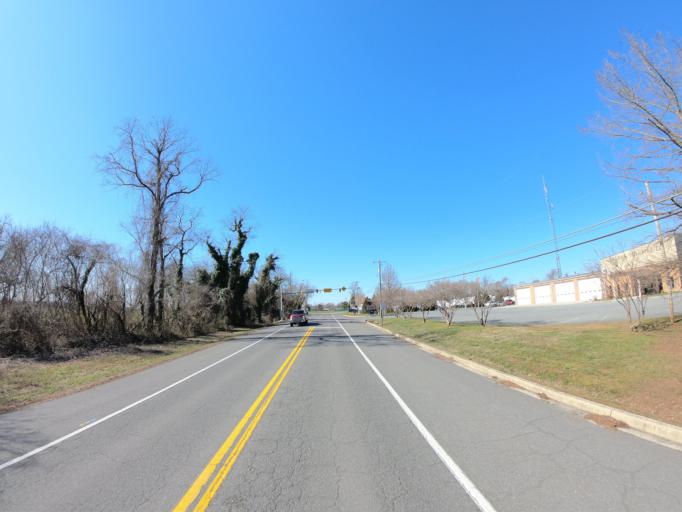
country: US
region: Delaware
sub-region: New Castle County
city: Townsend
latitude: 39.3416
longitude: -75.8716
